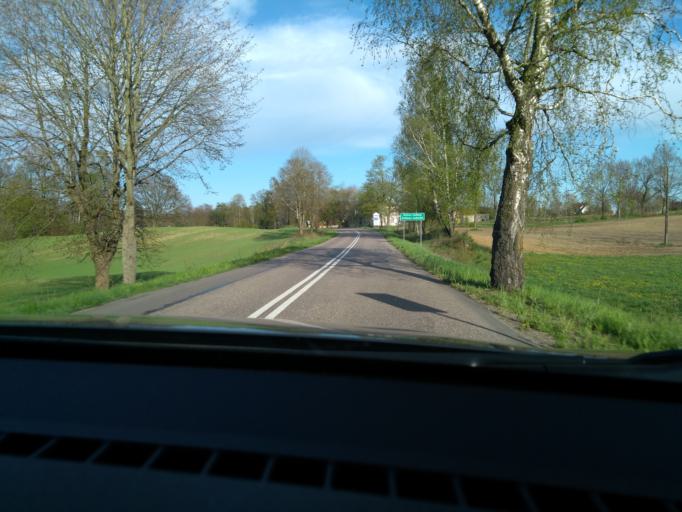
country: PL
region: Pomeranian Voivodeship
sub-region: Powiat leborski
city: Cewice
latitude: 54.3394
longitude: 17.7448
